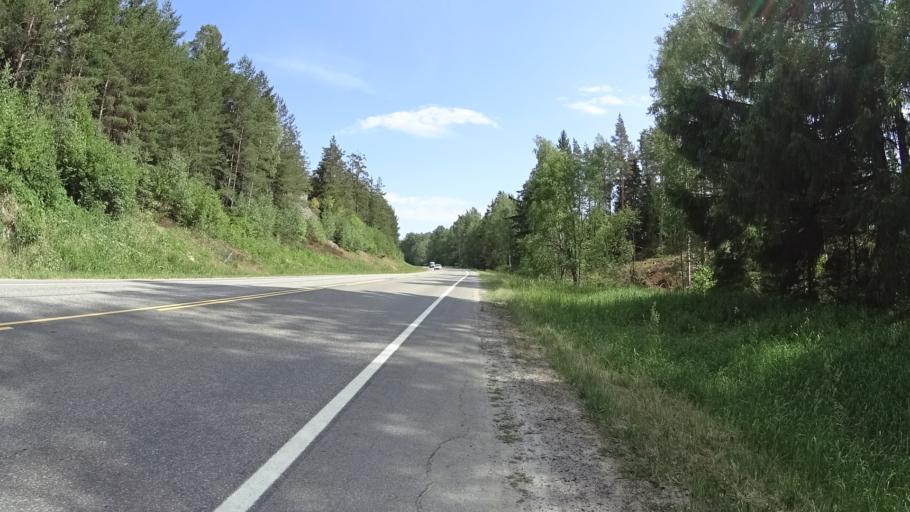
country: FI
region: Uusimaa
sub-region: Raaseporin
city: Pohja
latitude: 60.1013
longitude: 23.5780
